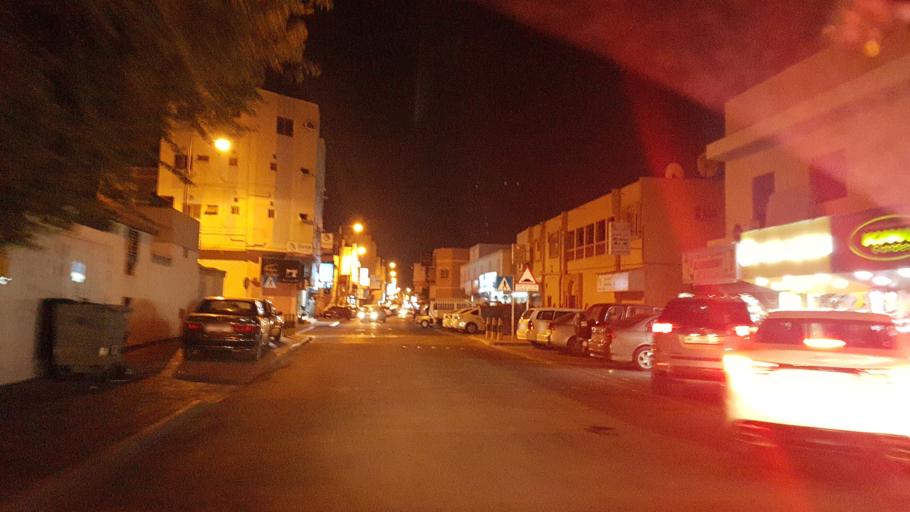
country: BH
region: Muharraq
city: Al Hadd
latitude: 26.2444
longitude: 50.6556
